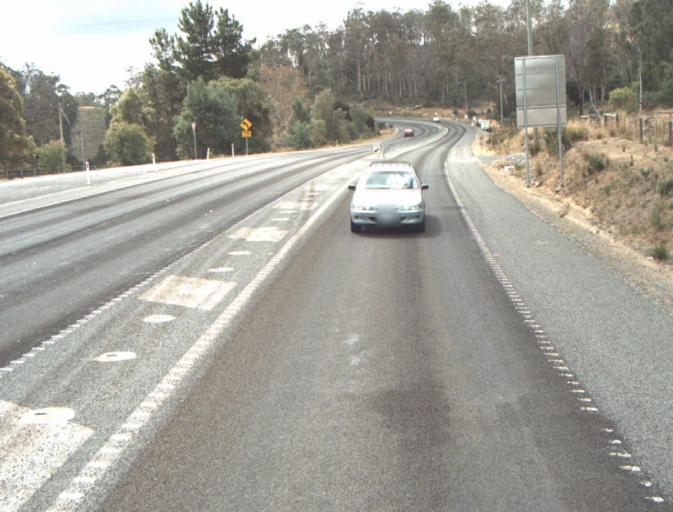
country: AU
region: Tasmania
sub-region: Launceston
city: Mayfield
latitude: -41.2948
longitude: 147.0485
